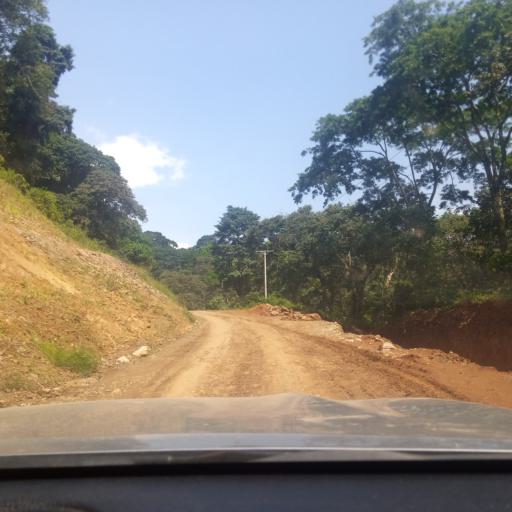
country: ET
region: Southern Nations, Nationalities, and People's Region
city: Tippi
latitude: 7.0709
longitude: 35.4331
